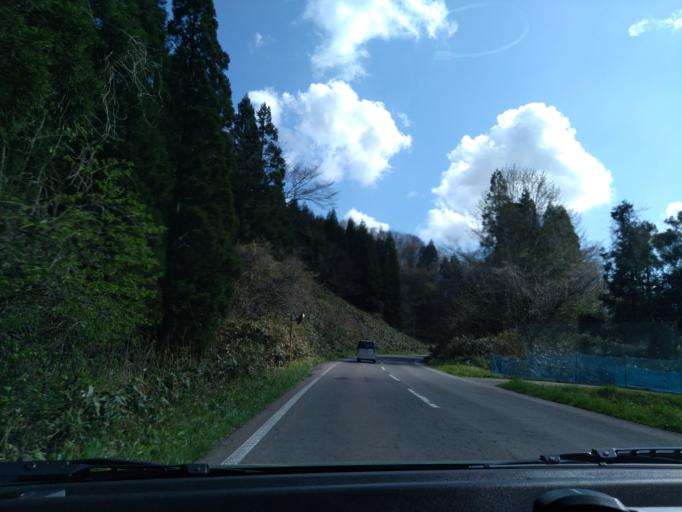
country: JP
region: Akita
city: Akita
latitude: 39.6926
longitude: 140.2284
